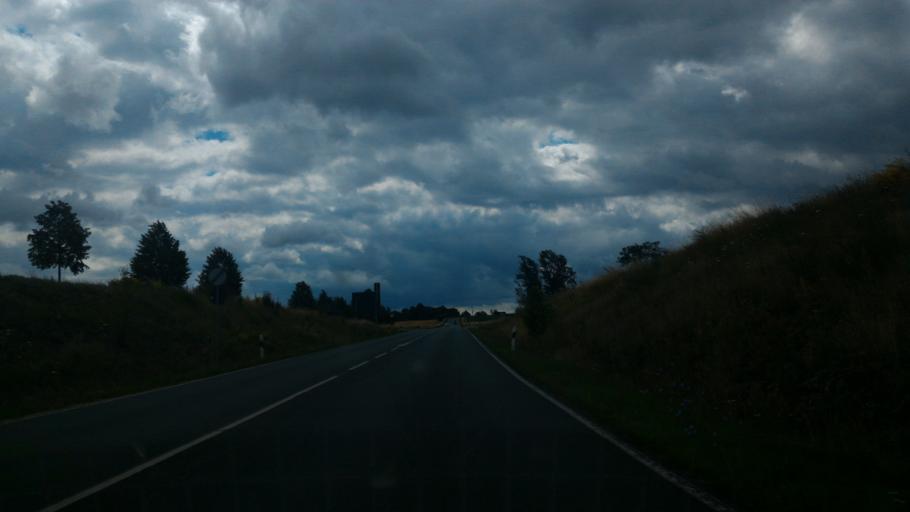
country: DE
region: Saxony
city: Kodersdorf
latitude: 51.2073
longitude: 14.9351
